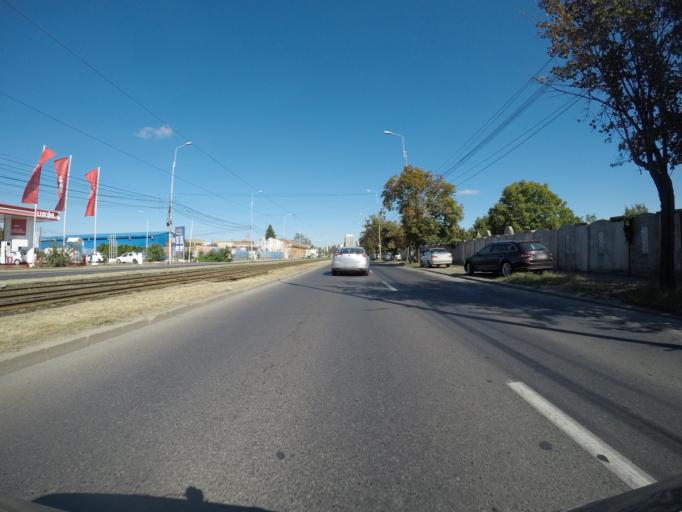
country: RO
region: Timis
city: Timisoara
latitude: 45.7461
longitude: 21.2544
